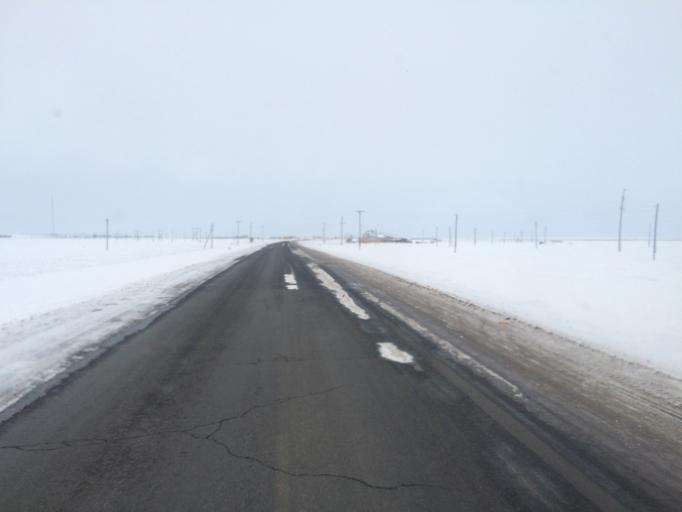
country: RU
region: Orenburg
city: Dombarovskiy
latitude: 49.9571
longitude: 60.0840
